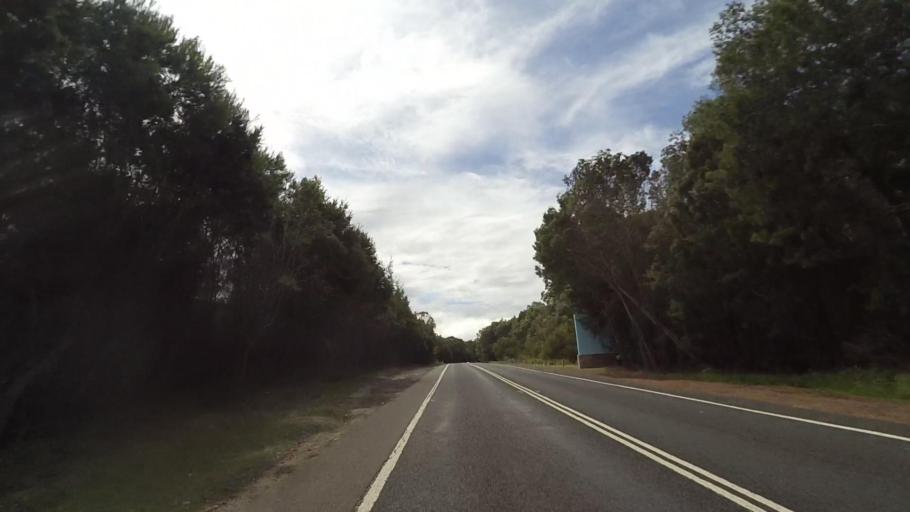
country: AU
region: New South Wales
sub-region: Sutherland Shire
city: Loftus
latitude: -34.0560
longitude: 151.0490
